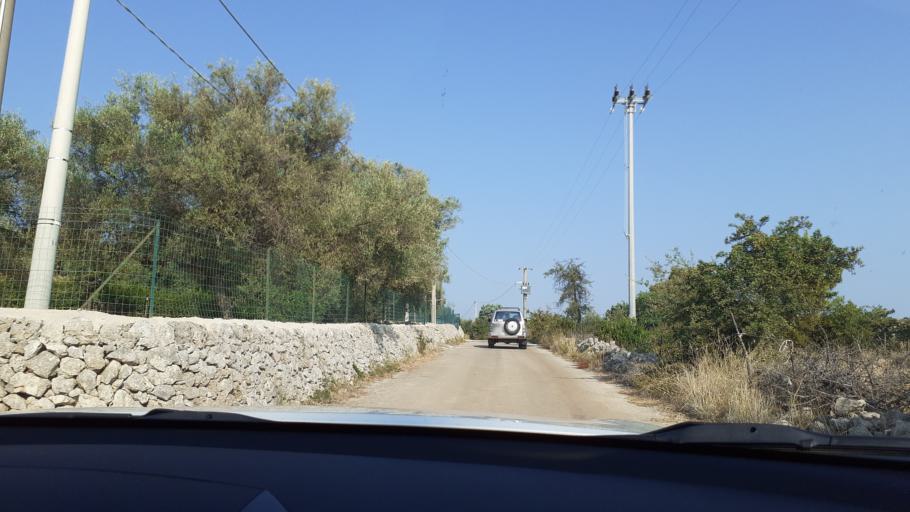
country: IT
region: Sicily
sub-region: Provincia di Siracusa
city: Cassibile
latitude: 36.9768
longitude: 15.1549
